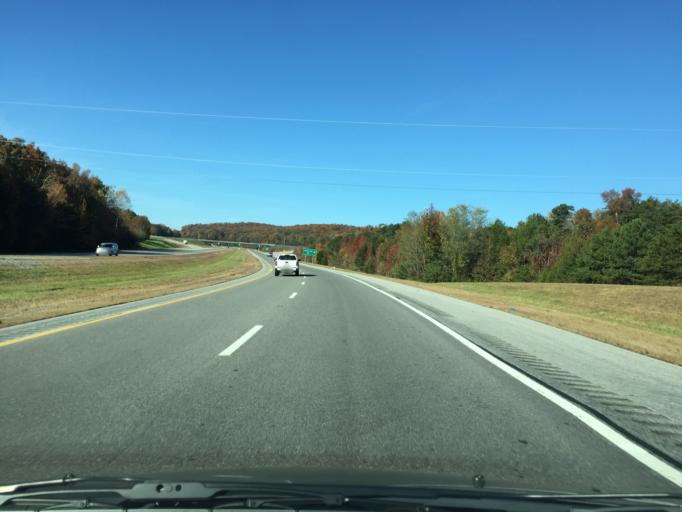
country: US
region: Tennessee
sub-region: Hamilton County
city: Sale Creek
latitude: 35.3453
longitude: -85.1744
